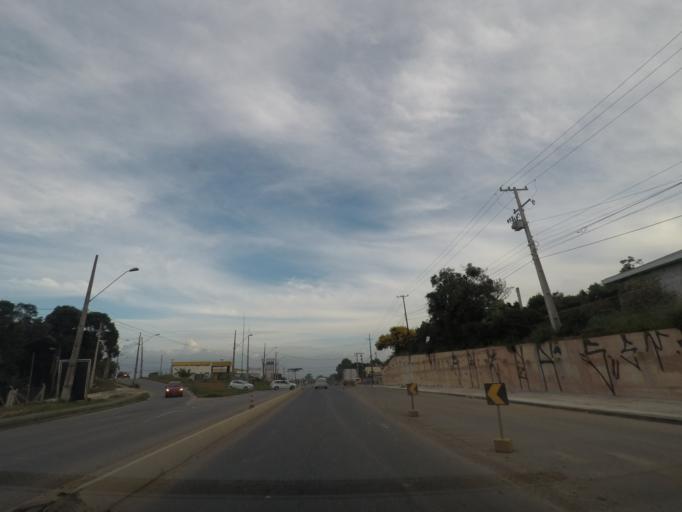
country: BR
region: Parana
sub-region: Colombo
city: Colombo
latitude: -25.3283
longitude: -49.2212
